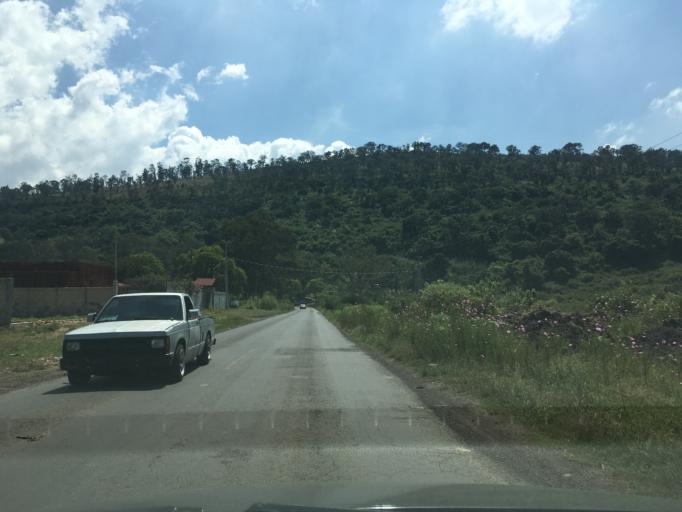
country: MX
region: Michoacan
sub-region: Morelia
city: La Mintzita (Piedra Dura)
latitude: 19.6420
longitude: -101.2780
